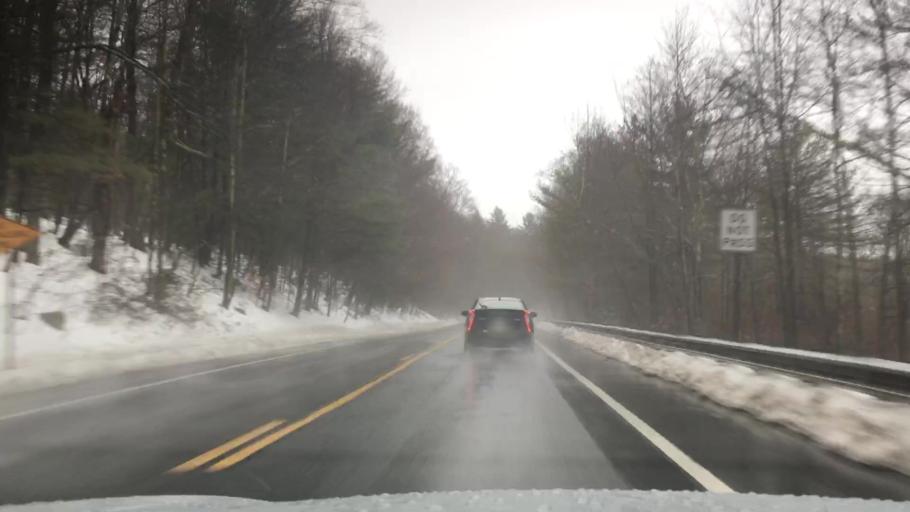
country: US
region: Massachusetts
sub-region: Franklin County
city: Shutesbury
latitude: 42.4461
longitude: -72.3881
